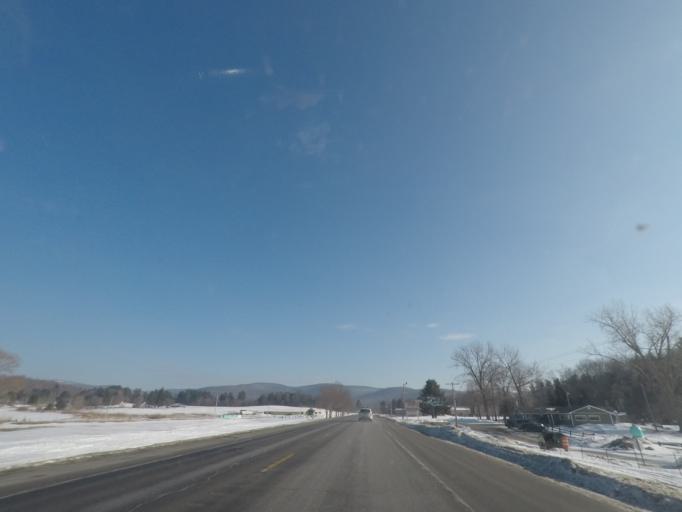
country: US
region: Massachusetts
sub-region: Berkshire County
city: Lanesborough
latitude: 42.5457
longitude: -73.3659
